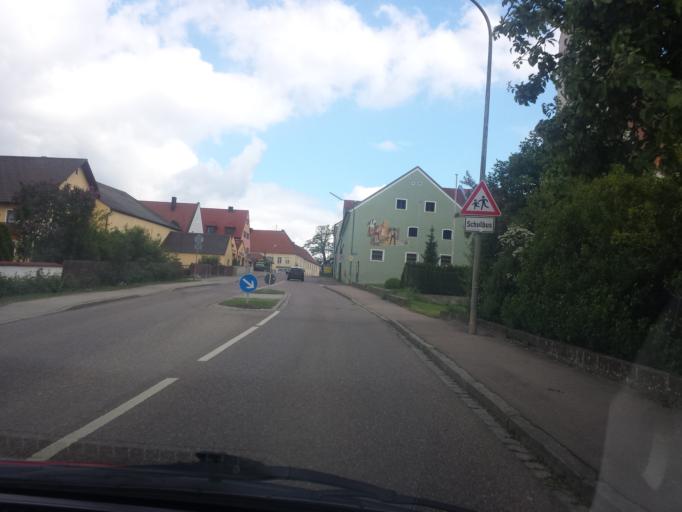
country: DE
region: Bavaria
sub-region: Upper Bavaria
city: Hepberg
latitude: 48.8215
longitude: 11.4619
